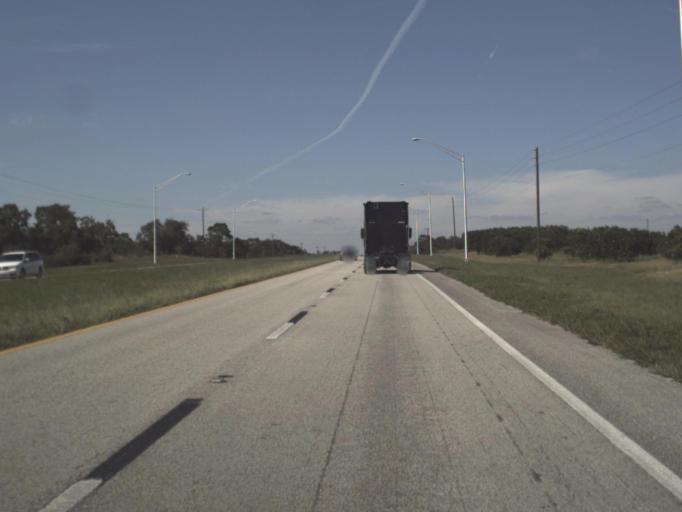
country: US
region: Florida
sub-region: Highlands County
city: Lake Placid
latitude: 27.3796
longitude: -81.4059
